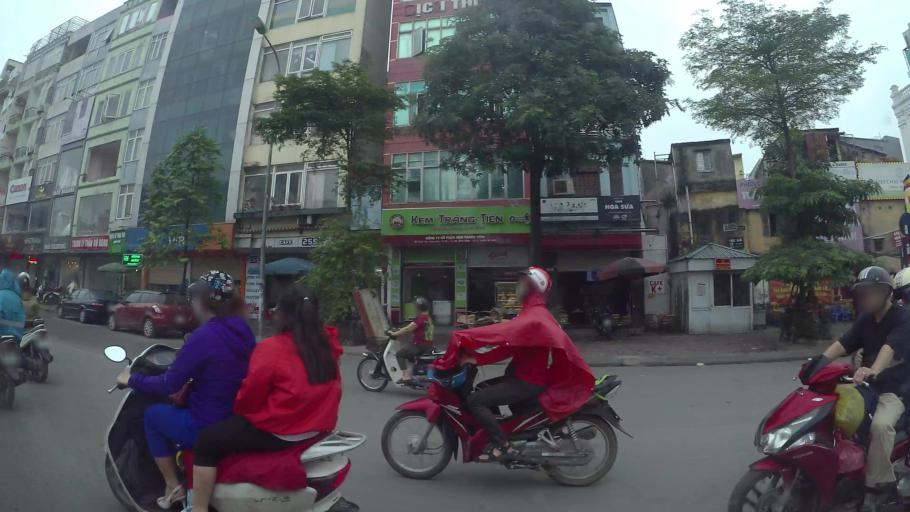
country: VN
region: Ha Noi
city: Dong Da
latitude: 21.0171
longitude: 105.8311
